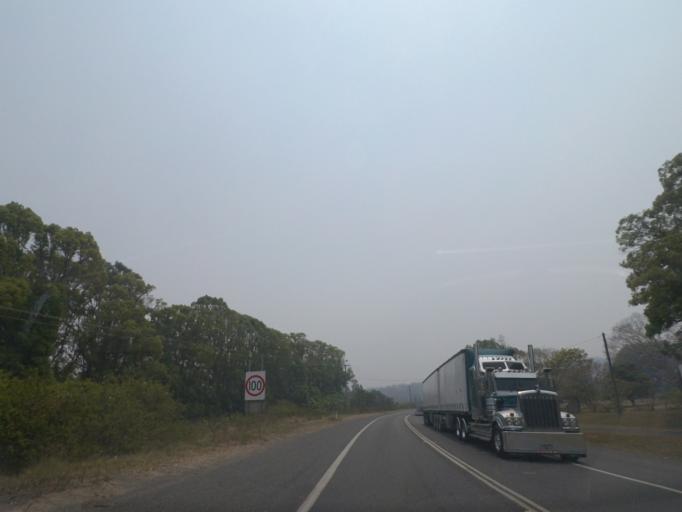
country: AU
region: New South Wales
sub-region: Clarence Valley
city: Maclean
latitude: -29.5458
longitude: 153.1557
